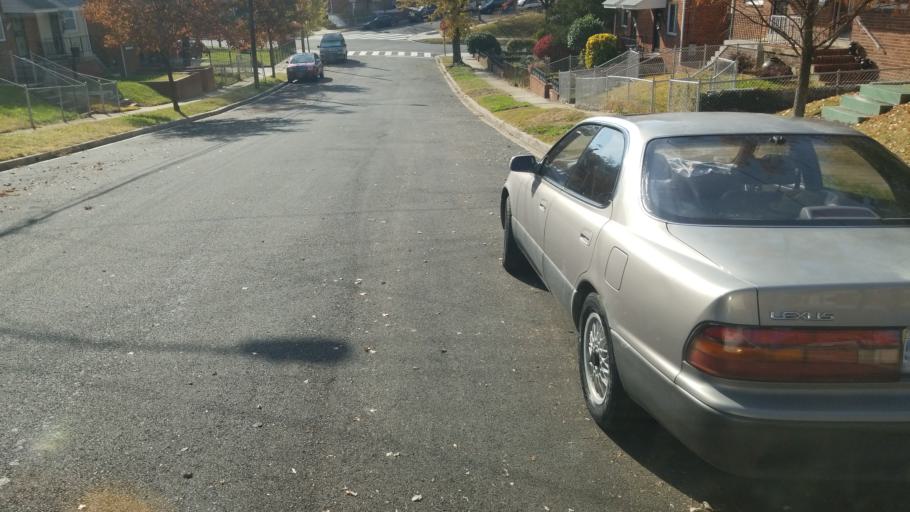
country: US
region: Maryland
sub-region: Prince George's County
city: Coral Hills
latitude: 38.8796
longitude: -76.9413
